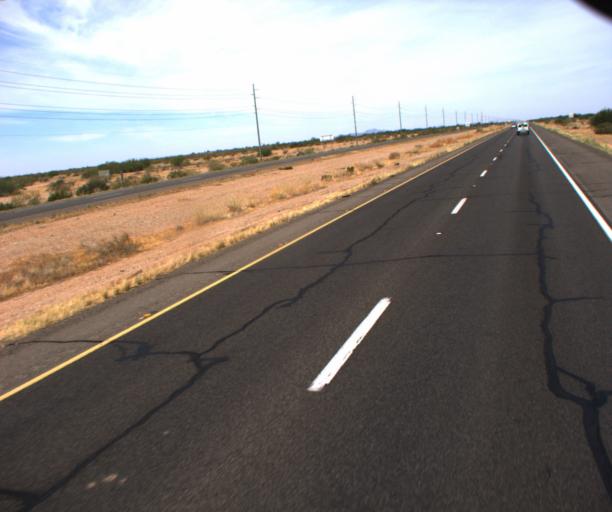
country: US
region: Arizona
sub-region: Maricopa County
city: Sun City West
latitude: 33.7154
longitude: -112.4483
